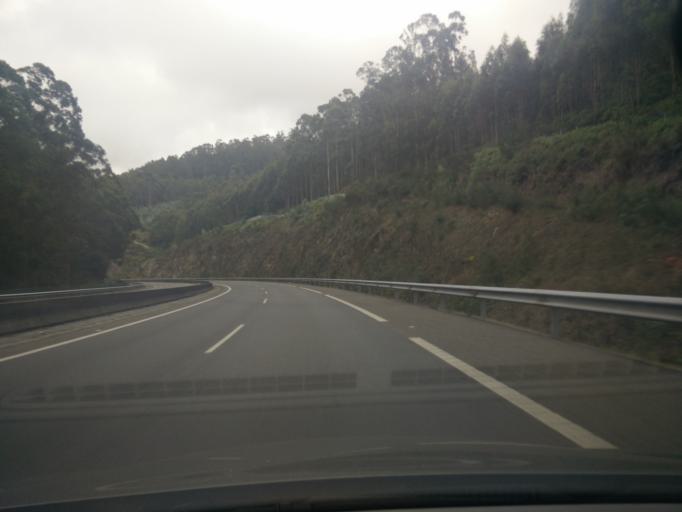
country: ES
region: Galicia
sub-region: Provincia da Coruna
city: Arteixo
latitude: 43.2816
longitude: -8.5174
